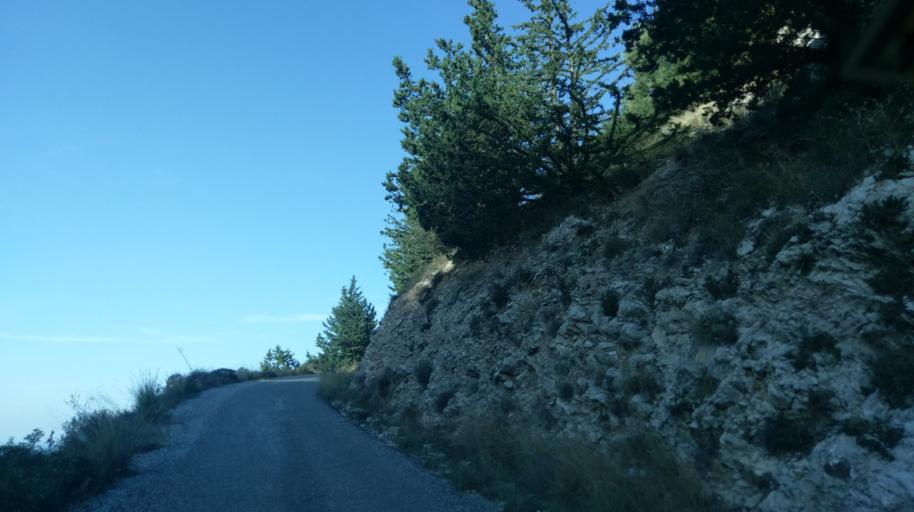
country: CY
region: Ammochostos
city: Lefkonoiko
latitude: 35.3344
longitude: 33.6320
